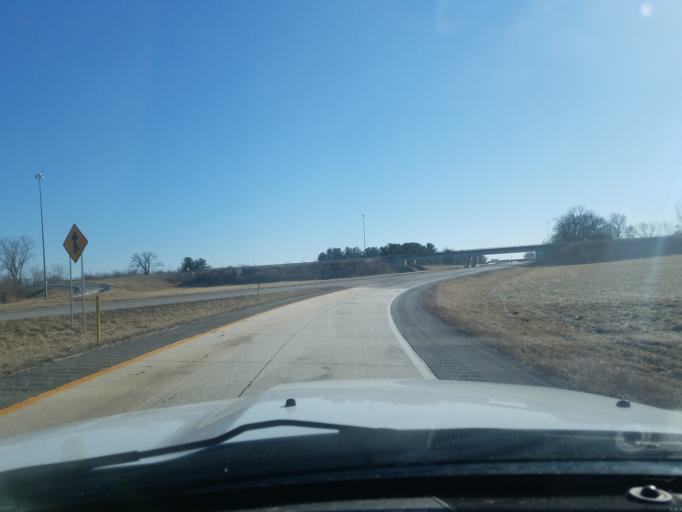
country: US
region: Kentucky
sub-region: Henderson County
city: Henderson
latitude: 37.8120
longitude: -87.5641
